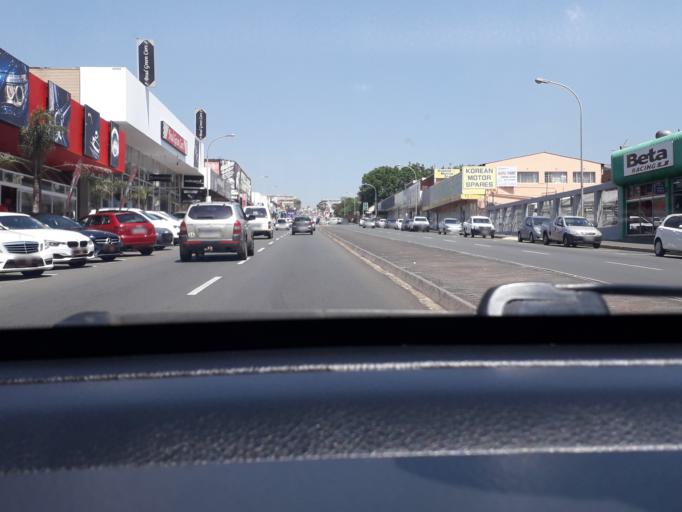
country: ZA
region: Gauteng
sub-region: City of Johannesburg Metropolitan Municipality
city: Modderfontein
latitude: -26.1330
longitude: 28.1484
